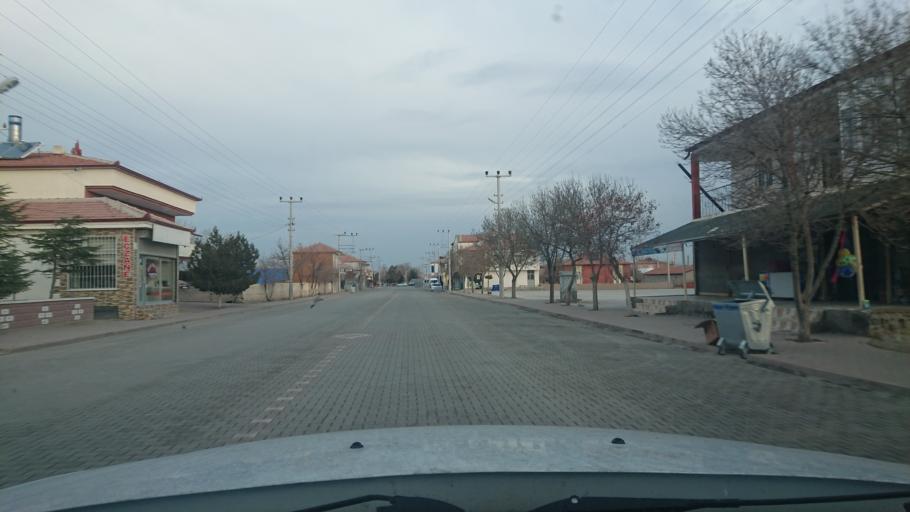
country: TR
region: Aksaray
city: Yesilova
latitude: 38.3407
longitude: 33.7503
